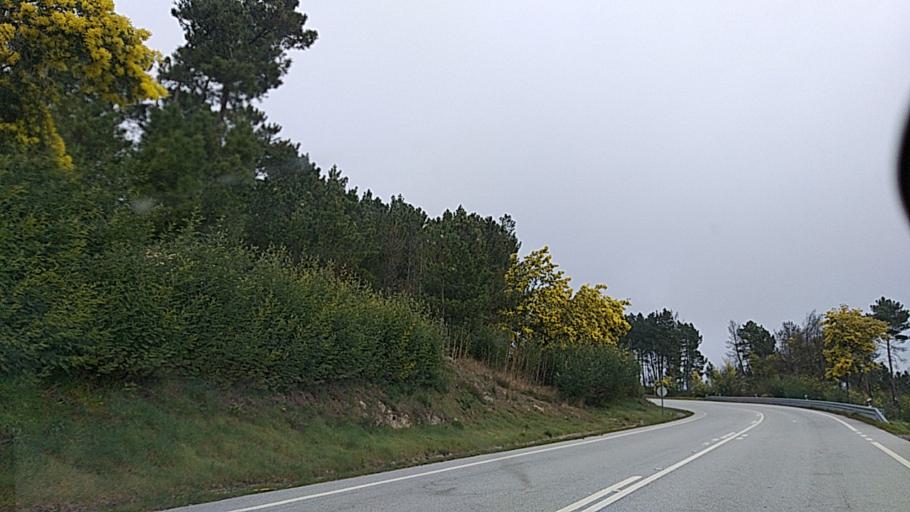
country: PT
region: Guarda
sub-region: Celorico da Beira
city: Celorico da Beira
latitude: 40.6898
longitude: -7.4684
